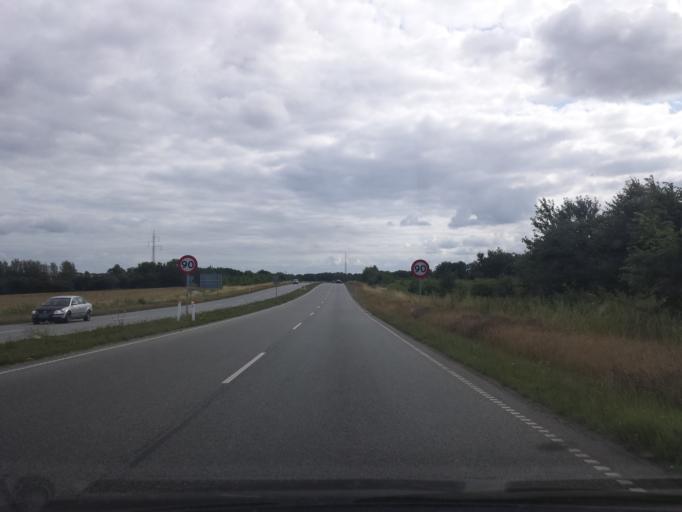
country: DK
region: South Denmark
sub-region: Sonderborg Kommune
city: Augustenborg
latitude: 54.9531
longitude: 9.8988
